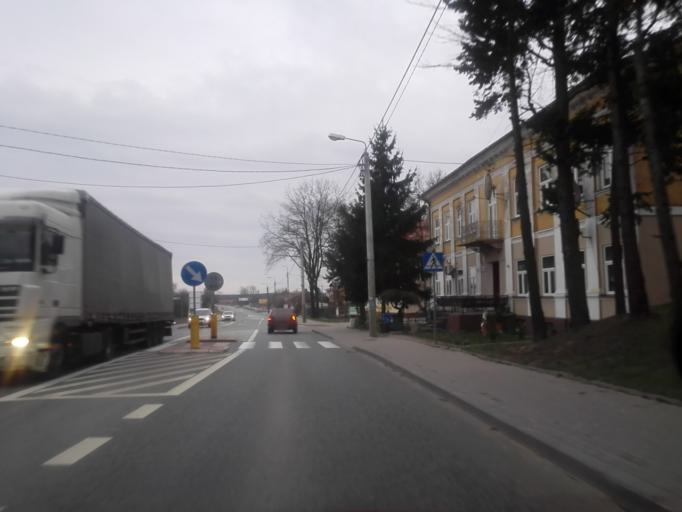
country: PL
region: Podlasie
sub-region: Powiat grajewski
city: Rajgrod
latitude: 53.7287
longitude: 22.6870
